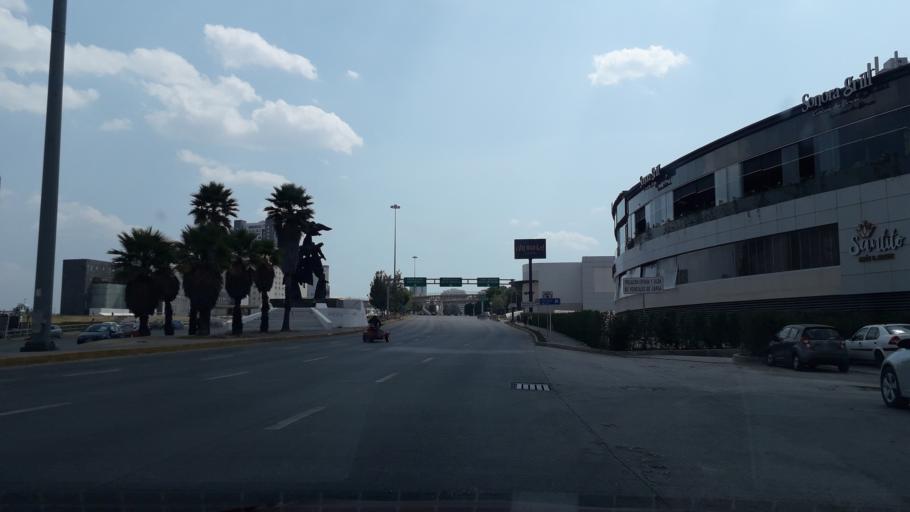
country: MX
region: Puebla
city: Puebla
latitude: 19.0349
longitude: -98.2273
